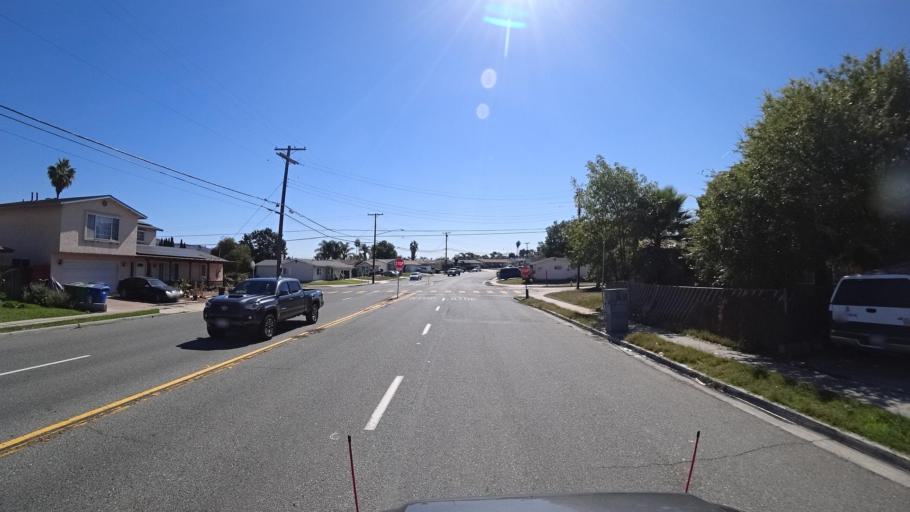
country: US
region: California
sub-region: San Diego County
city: La Presa
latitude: 32.7063
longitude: -117.0139
